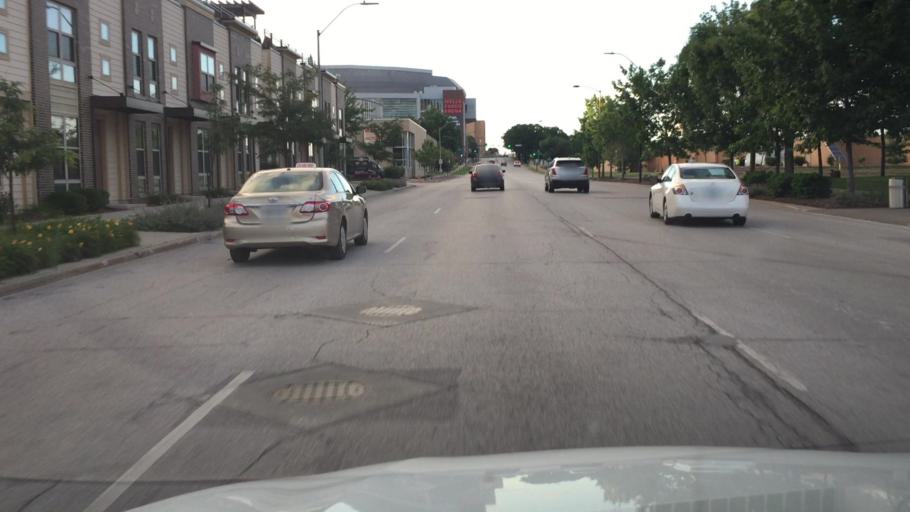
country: US
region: Iowa
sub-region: Polk County
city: Des Moines
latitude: 41.5890
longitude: -93.6204
